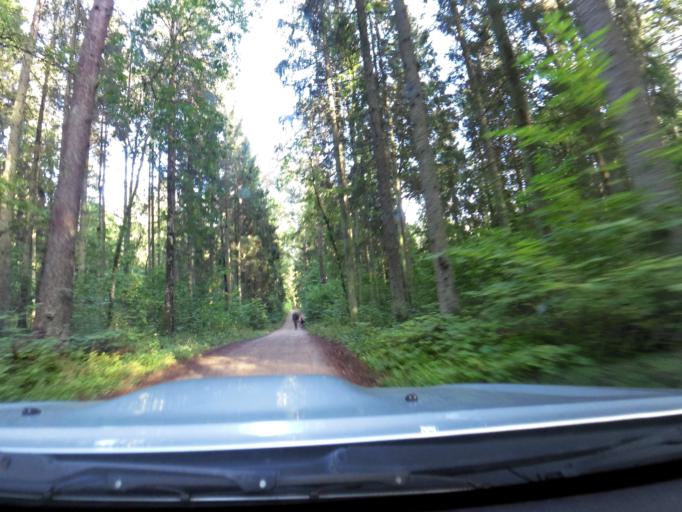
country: LT
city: Trakai
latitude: 54.6471
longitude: 24.9694
